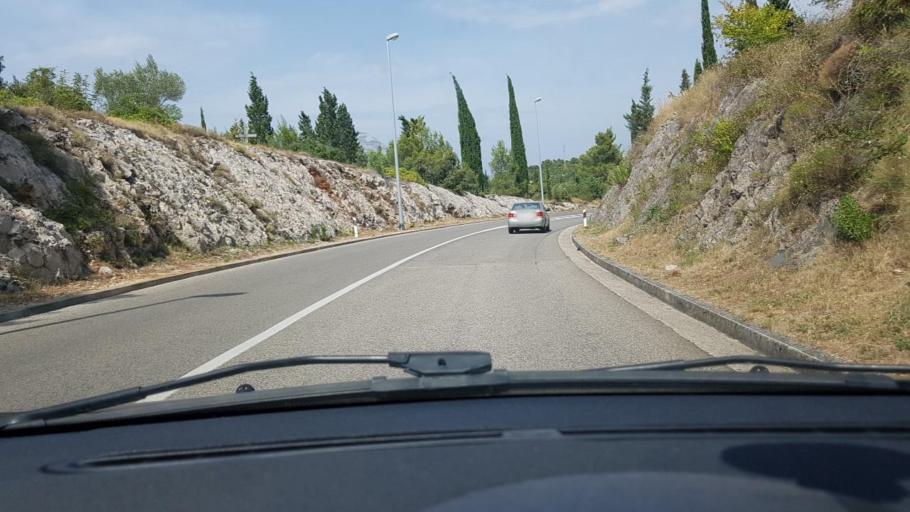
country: HR
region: Dubrovacko-Neretvanska
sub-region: Grad Korcula
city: Zrnovo
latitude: 42.9449
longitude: 17.1085
